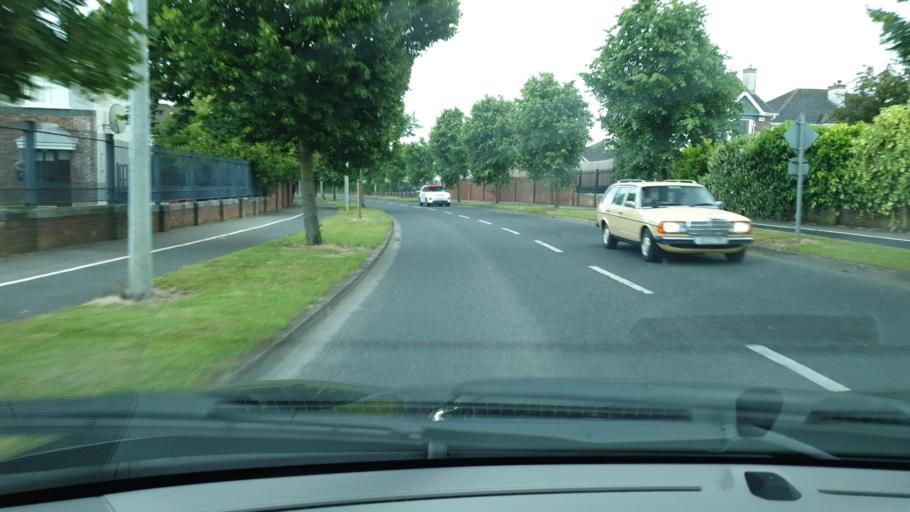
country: IE
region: Leinster
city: Lucan
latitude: 53.3420
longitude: -6.4461
